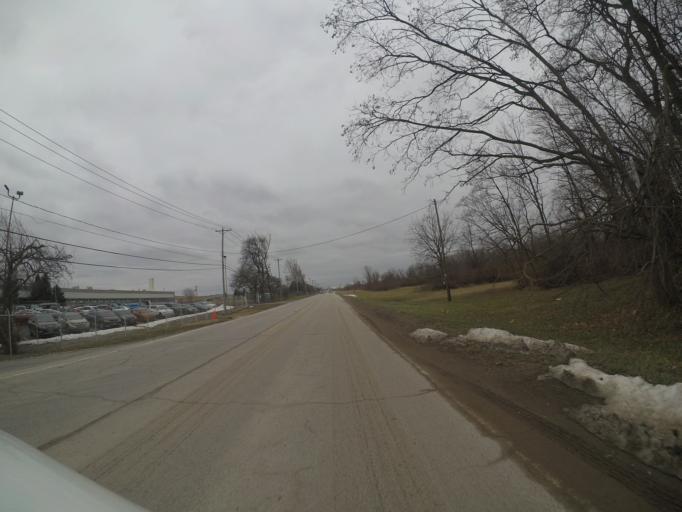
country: US
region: Ohio
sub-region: Wood County
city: Walbridge
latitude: 41.6115
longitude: -83.5125
